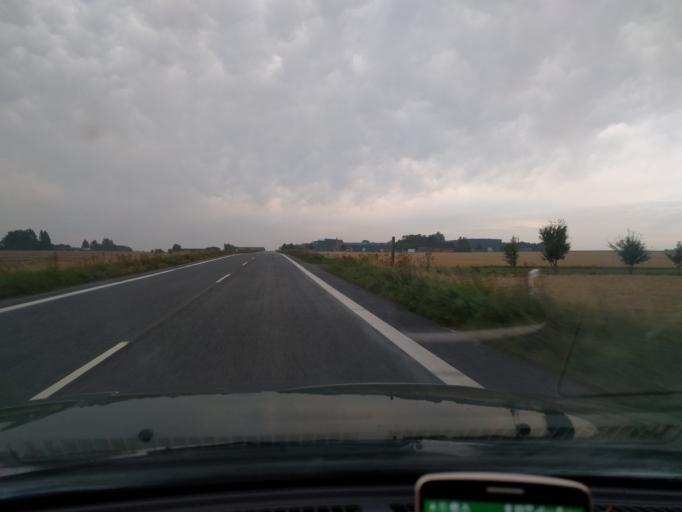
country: DK
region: Zealand
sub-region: Guldborgsund Kommune
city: Norre Alslev
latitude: 54.9150
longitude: 11.8764
